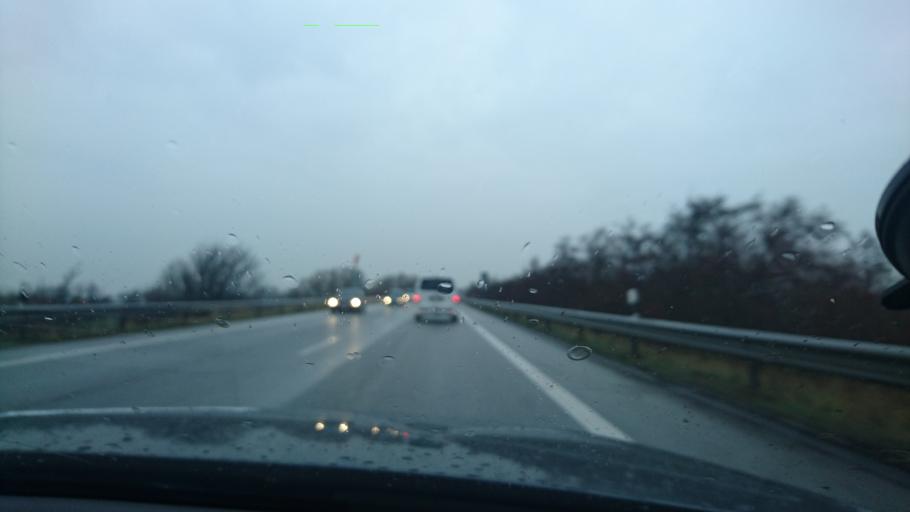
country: DE
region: Schleswig-Holstein
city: Grossenbrode
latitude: 54.4132
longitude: 11.1201
